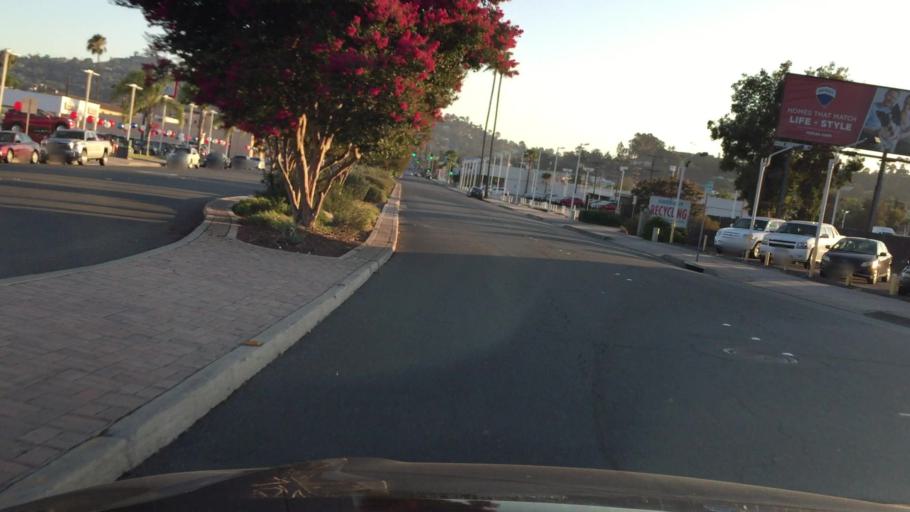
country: US
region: California
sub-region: San Diego County
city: El Cajon
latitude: 32.7944
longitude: -116.9684
